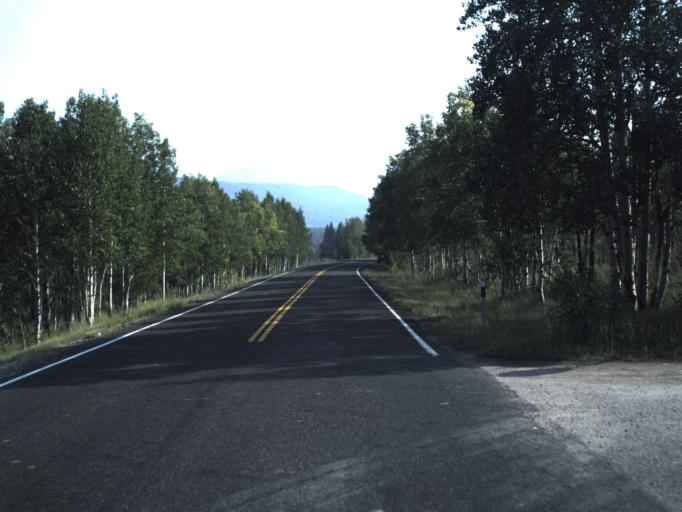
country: US
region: Wyoming
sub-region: Uinta County
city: Evanston
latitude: 40.8413
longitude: -110.8476
